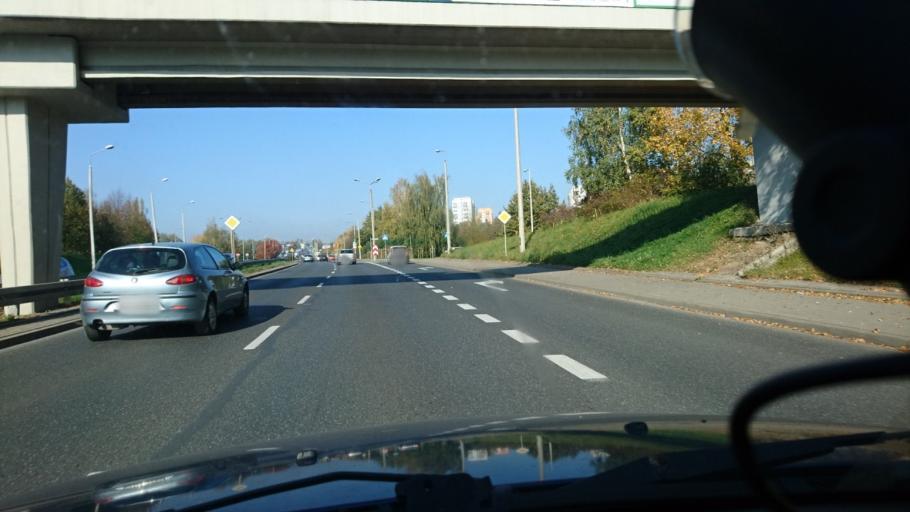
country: PL
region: Silesian Voivodeship
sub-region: Bielsko-Biala
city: Bielsko-Biala
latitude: 49.8086
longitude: 19.0287
